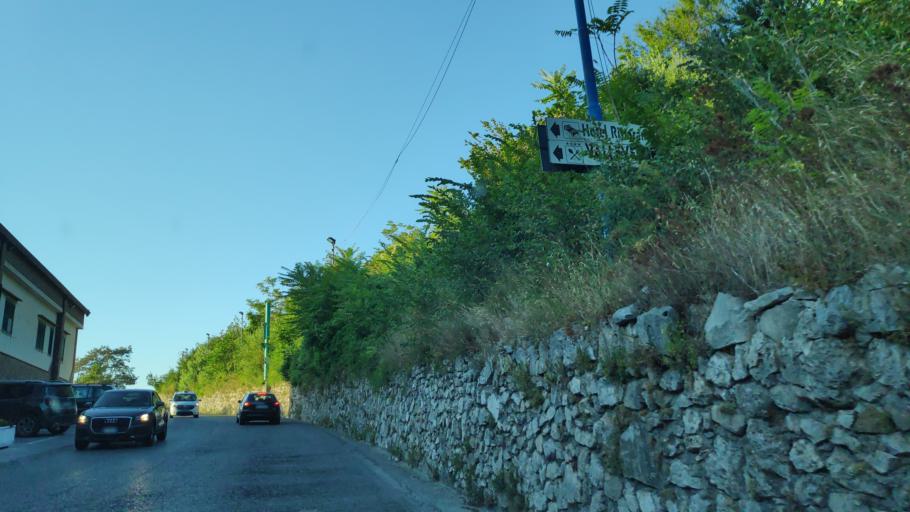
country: IT
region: Campania
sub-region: Provincia di Salerno
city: Corbara
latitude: 40.7231
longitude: 14.6016
